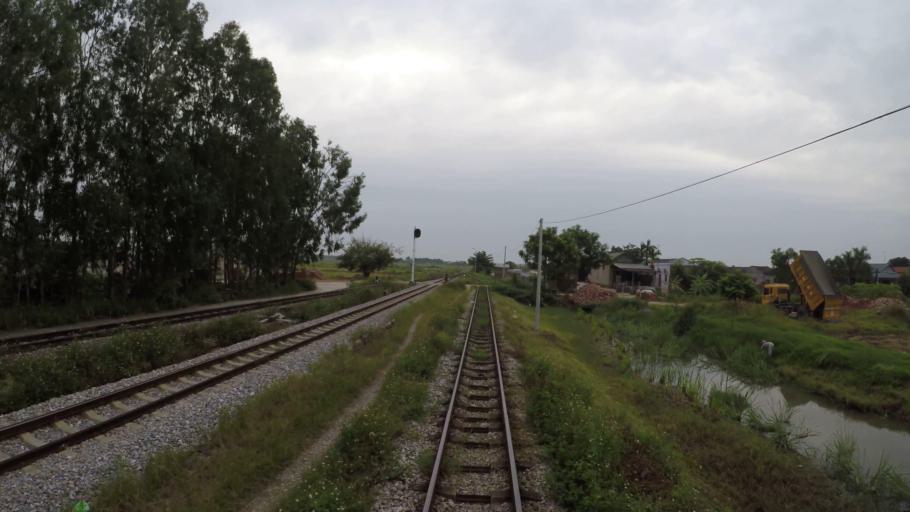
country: VN
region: Hai Duong
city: Ke Sat
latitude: 20.9676
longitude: 106.1682
